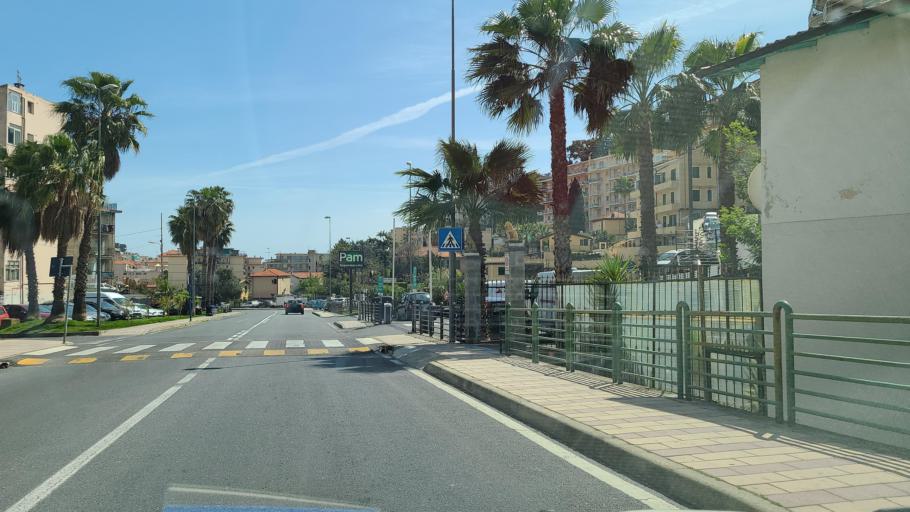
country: IT
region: Liguria
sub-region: Provincia di Imperia
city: San Remo
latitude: 43.8236
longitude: 7.7646
